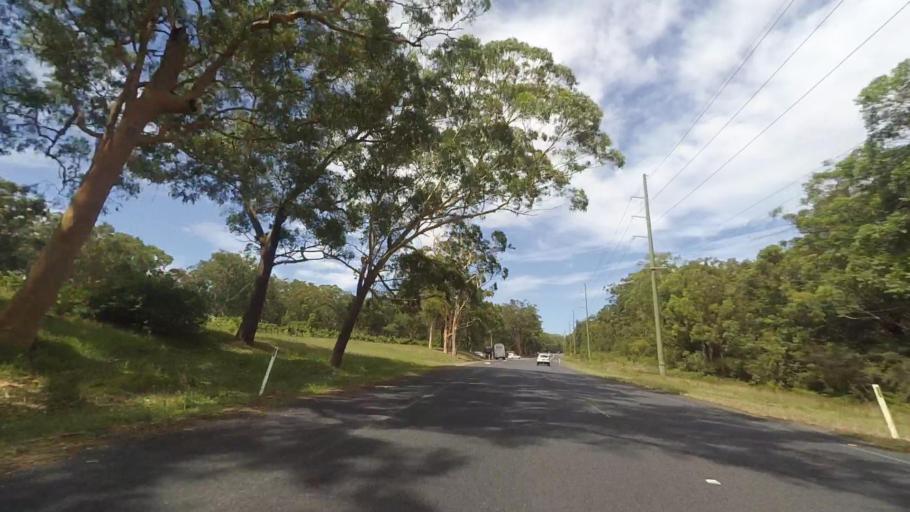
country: AU
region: New South Wales
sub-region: Port Stephens Shire
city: Anna Bay
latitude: -32.7812
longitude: 151.9848
